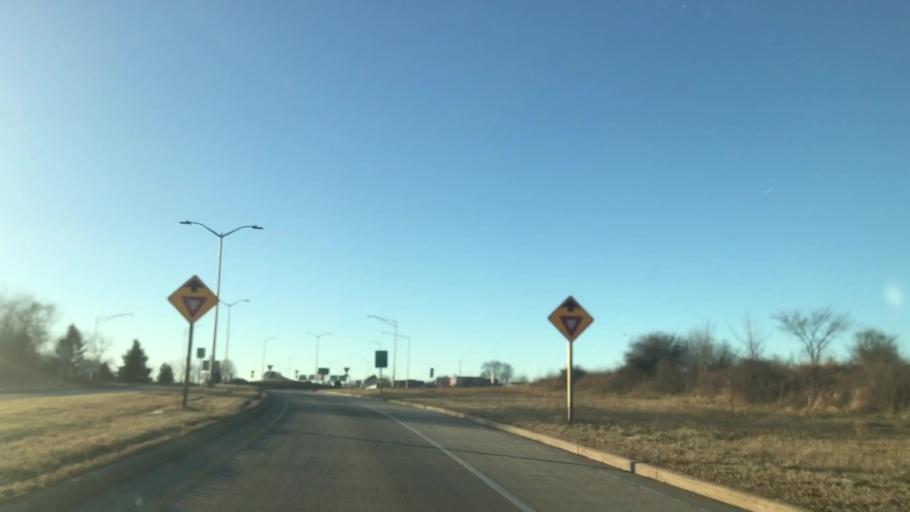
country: US
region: Wisconsin
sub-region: Washington County
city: Richfield
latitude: 43.2839
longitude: -88.1833
